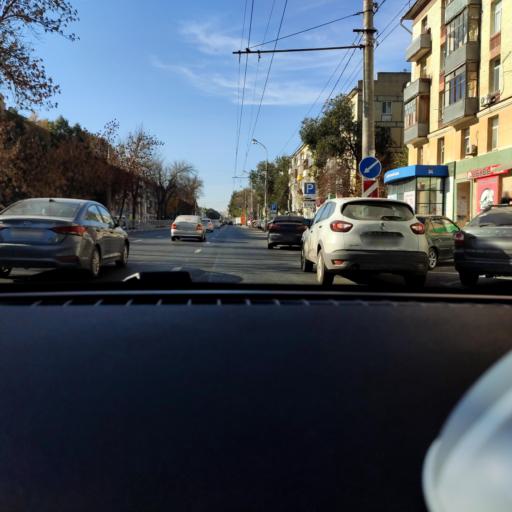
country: RU
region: Samara
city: Samara
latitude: 53.2097
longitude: 50.2415
